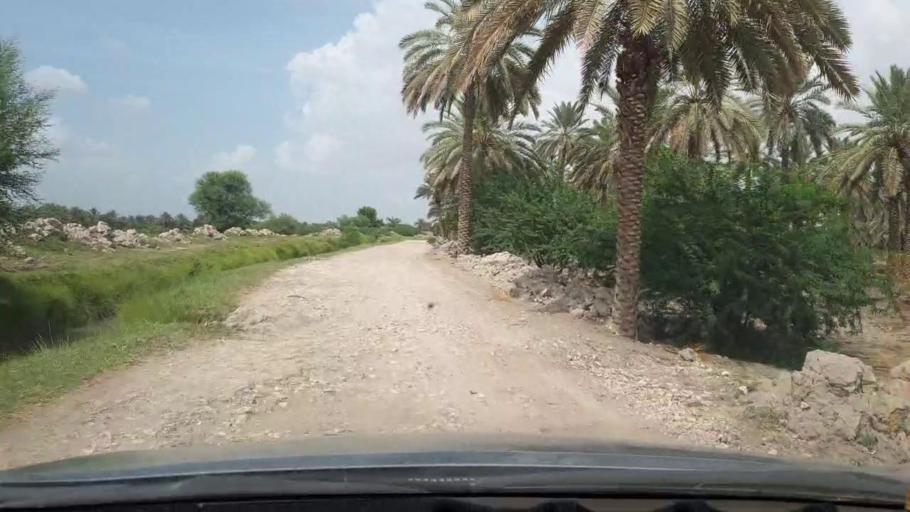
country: PK
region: Sindh
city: Khairpur
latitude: 27.4718
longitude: 68.8468
